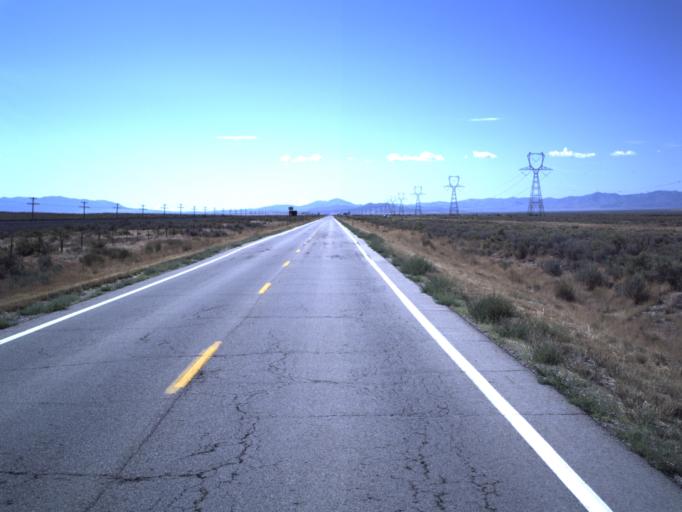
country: US
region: Utah
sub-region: Tooele County
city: Tooele
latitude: 40.3433
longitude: -112.4108
